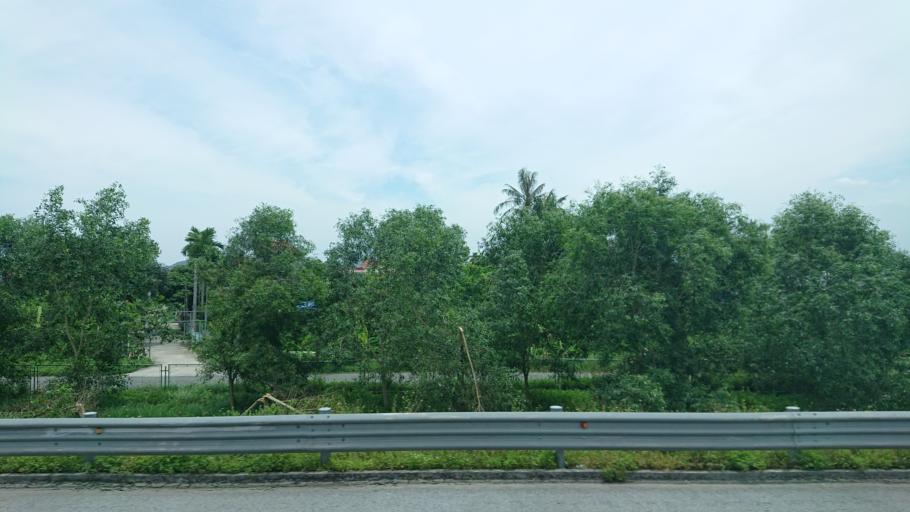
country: VN
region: Hai Phong
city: Nui Doi
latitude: 20.7678
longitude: 106.6371
